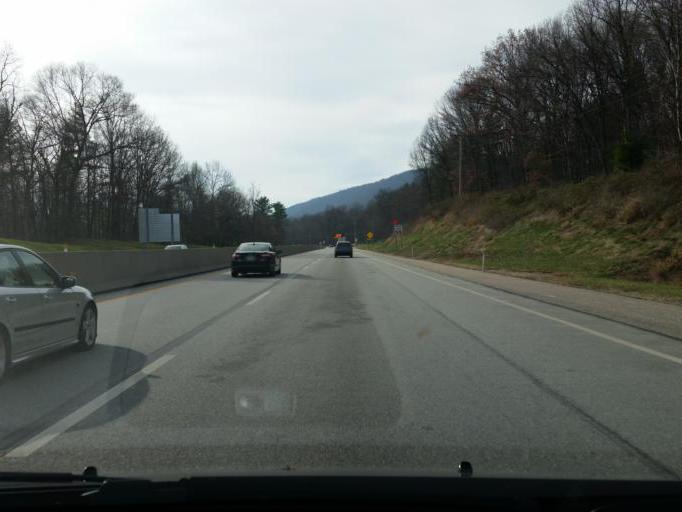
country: US
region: Pennsylvania
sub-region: Franklin County
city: Doylestown
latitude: 40.0938
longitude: -77.8206
